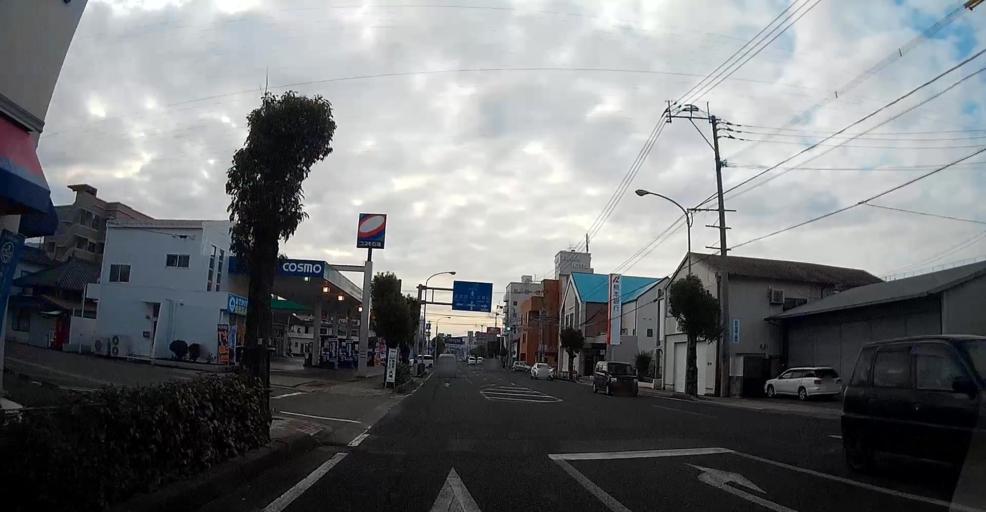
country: JP
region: Kumamoto
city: Hondo
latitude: 32.4564
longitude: 130.1935
